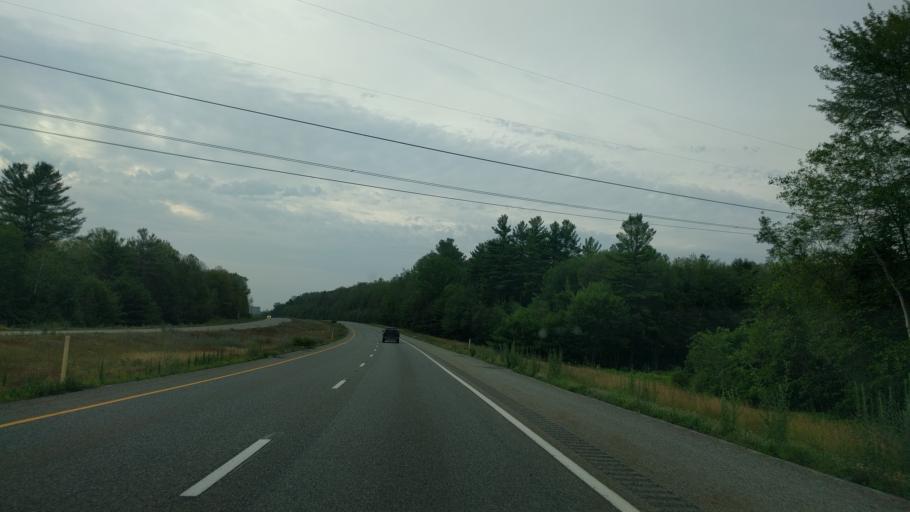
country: US
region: Massachusetts
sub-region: Worcester County
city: Millville
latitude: 42.0326
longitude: -71.6192
